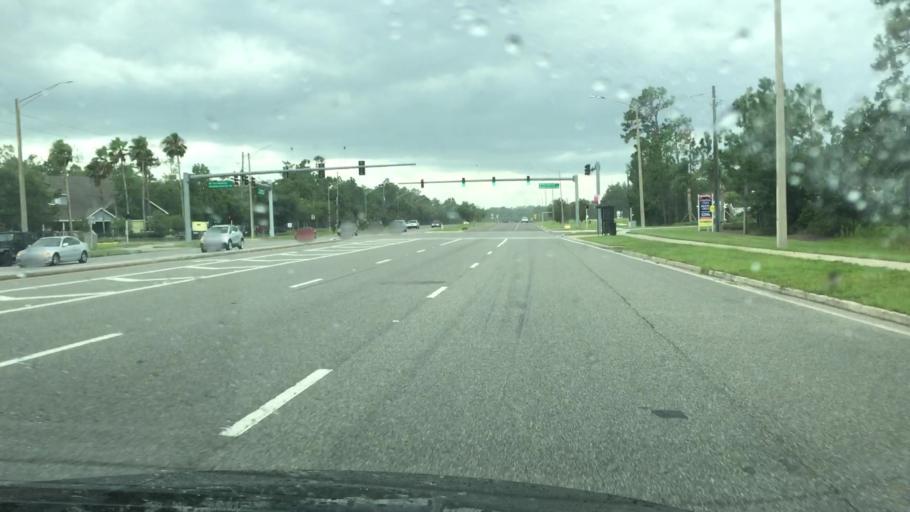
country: US
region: Florida
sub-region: Duval County
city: Jacksonville Beach
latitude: 30.2816
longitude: -81.4918
